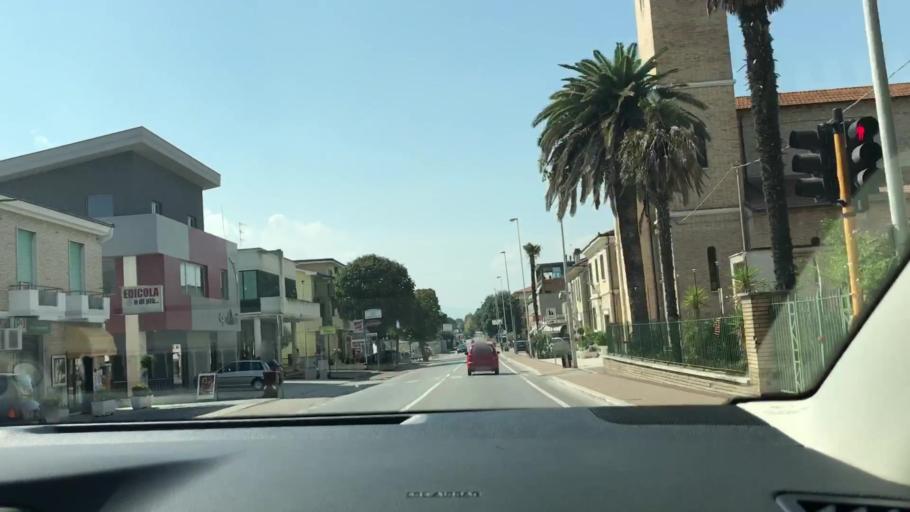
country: IT
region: The Marches
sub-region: Provincia di Ascoli Piceno
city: Centobuchi
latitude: 42.8979
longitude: 13.8506
